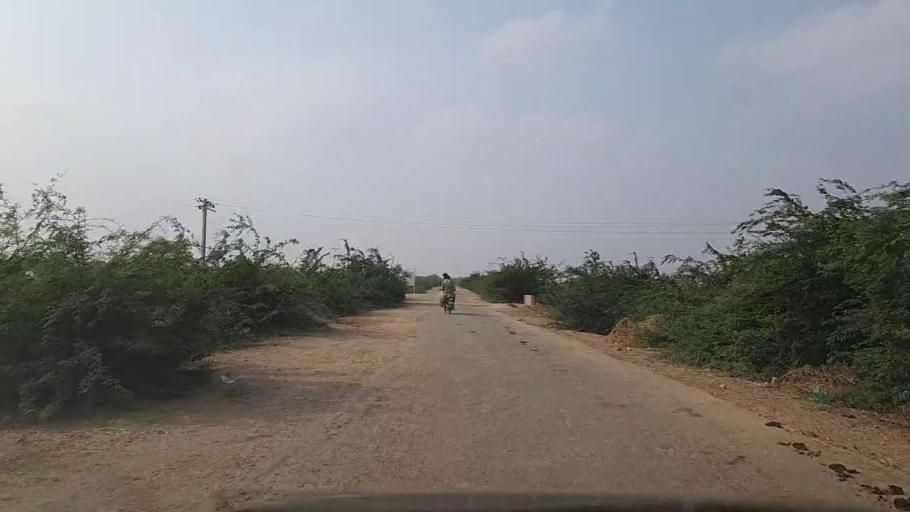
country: PK
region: Sindh
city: Thatta
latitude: 24.8579
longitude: 67.7775
